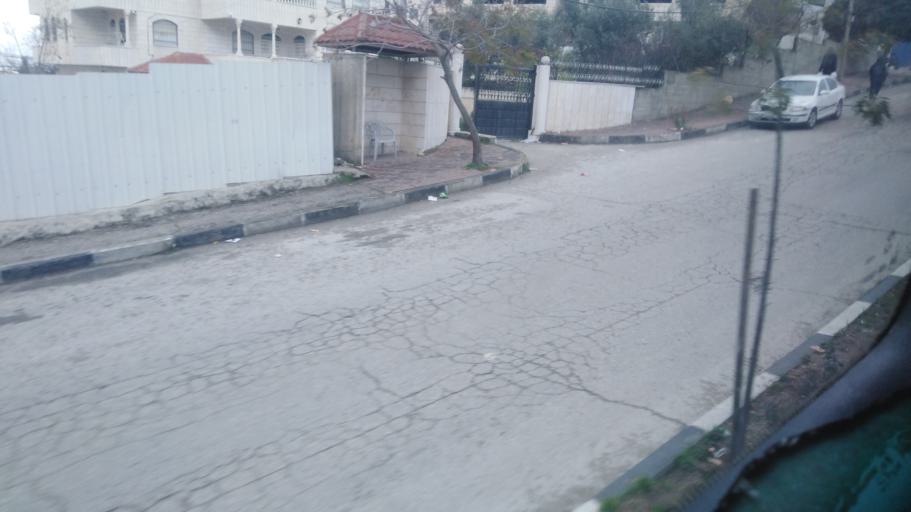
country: PS
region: West Bank
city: Hebron
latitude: 31.5291
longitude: 35.0839
